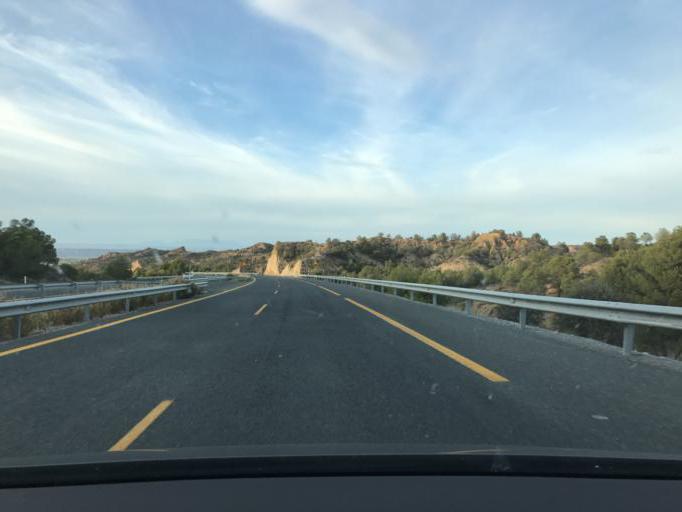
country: ES
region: Andalusia
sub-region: Provincia de Granada
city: Guadix
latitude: 37.2793
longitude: -3.0965
